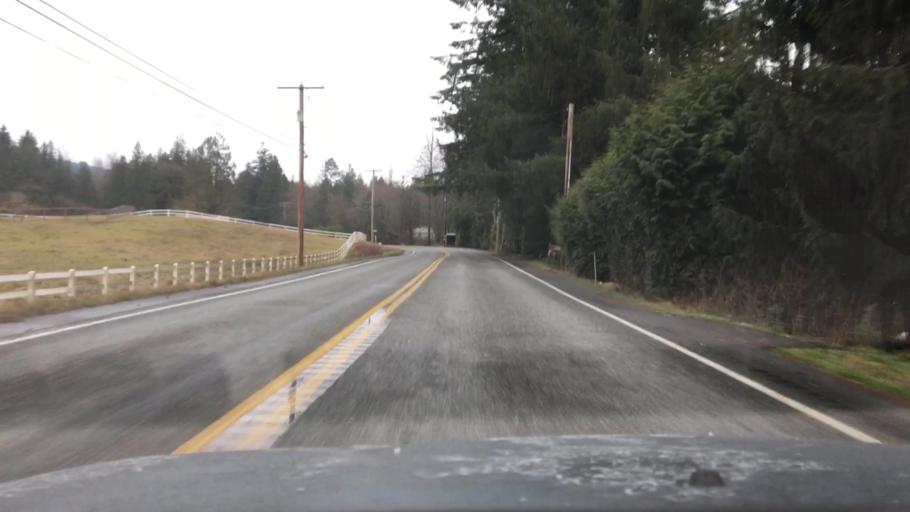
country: US
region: Washington
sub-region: Whatcom County
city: Sudden Valley
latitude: 48.6478
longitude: -122.3242
